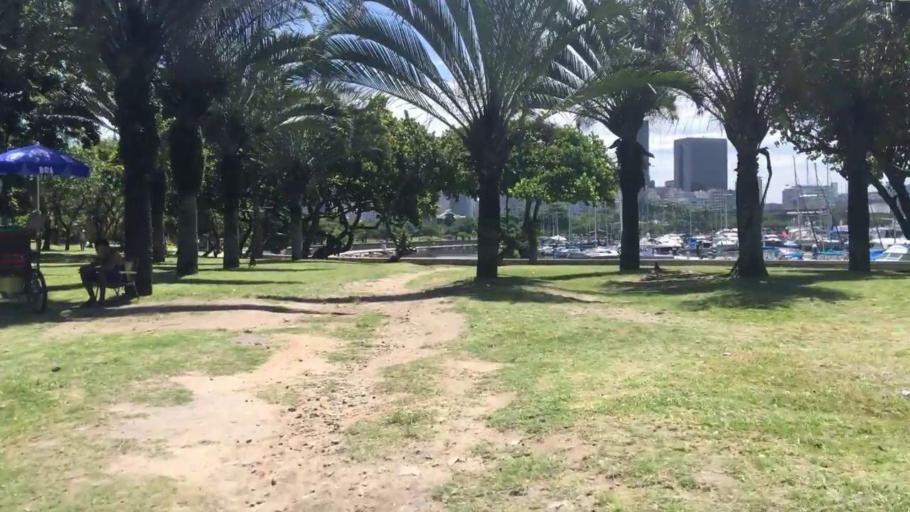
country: BR
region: Rio de Janeiro
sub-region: Rio De Janeiro
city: Rio de Janeiro
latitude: -22.9201
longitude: -43.1717
